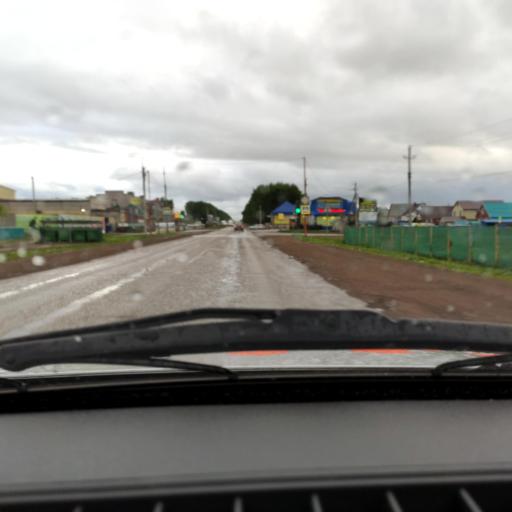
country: RU
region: Bashkortostan
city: Sterlitamak
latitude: 53.5927
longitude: 55.9080
